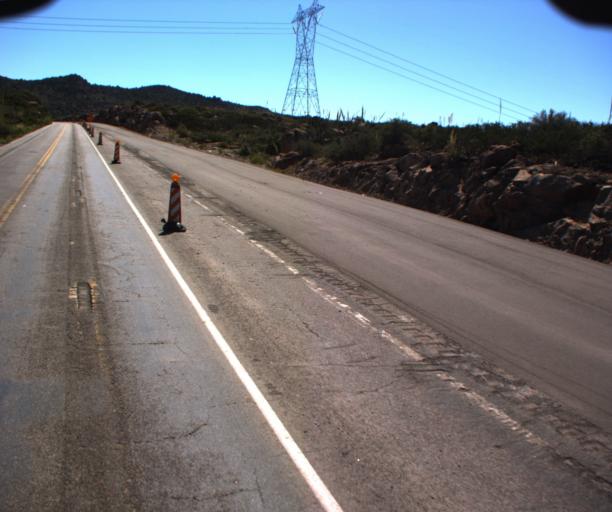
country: US
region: Arizona
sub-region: Pinal County
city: Superior
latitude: 33.3146
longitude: -111.0407
